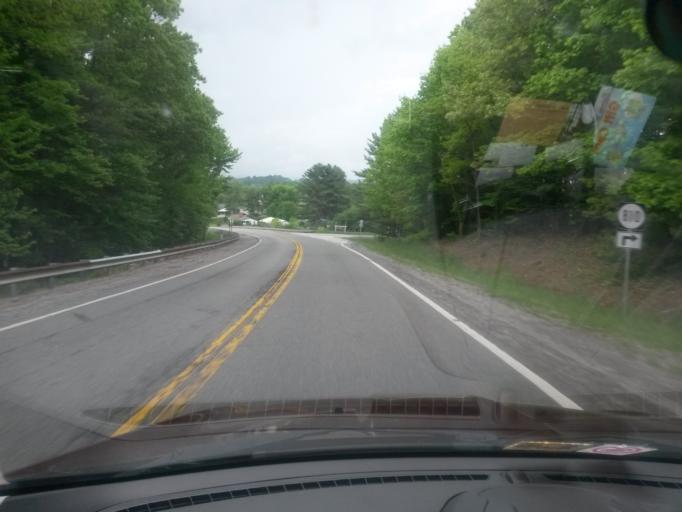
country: US
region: Virginia
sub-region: Floyd County
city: Floyd
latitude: 36.9503
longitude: -80.3599
